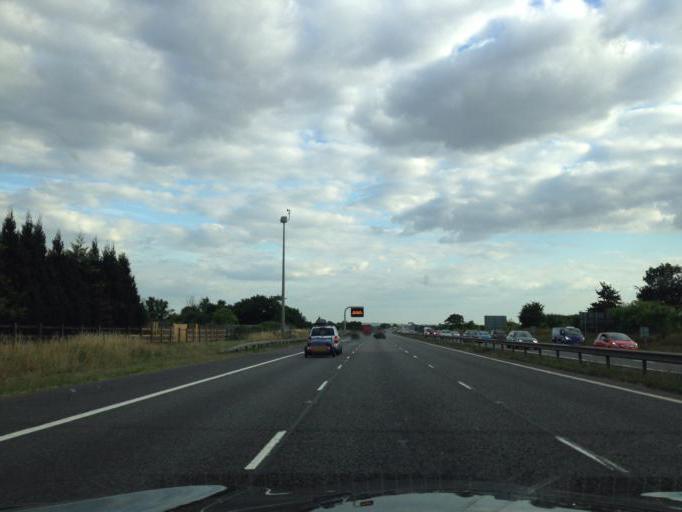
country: GB
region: England
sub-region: Oxfordshire
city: Bicester
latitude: 51.9400
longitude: -1.2020
